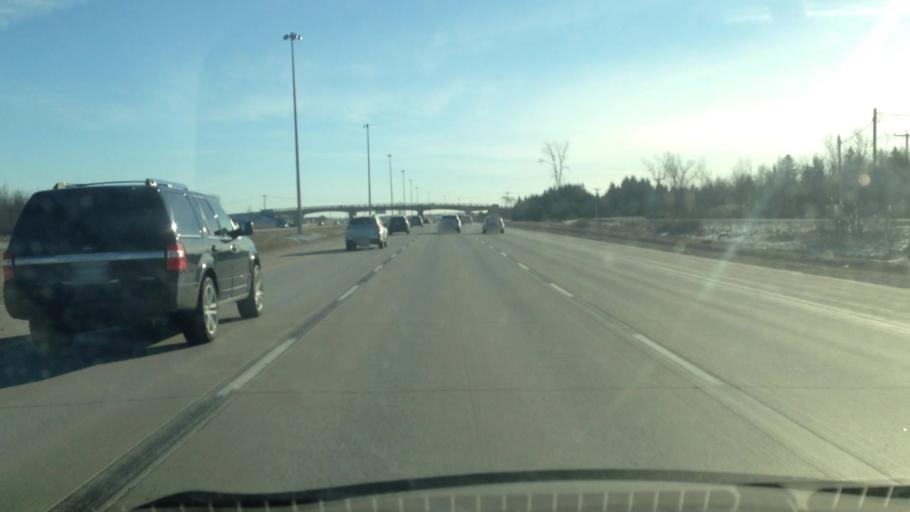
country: CA
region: Quebec
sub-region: Laurentides
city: Saint-Jerome
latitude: 45.7385
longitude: -73.9922
